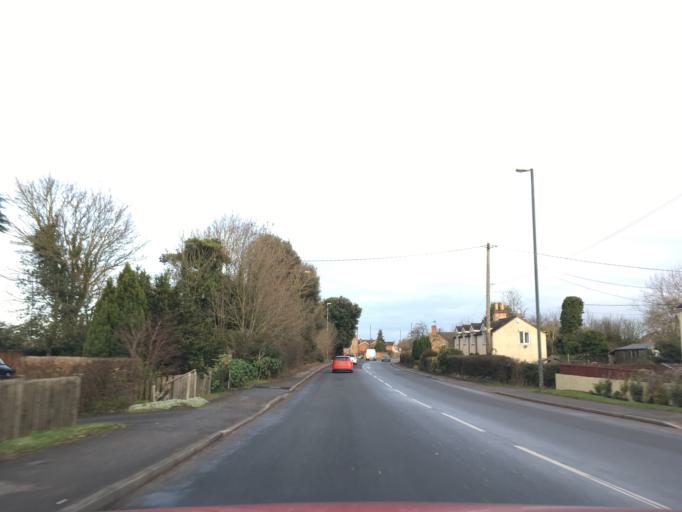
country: GB
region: England
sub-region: Gloucestershire
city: Stonehouse
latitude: 51.8121
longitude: -2.2846
